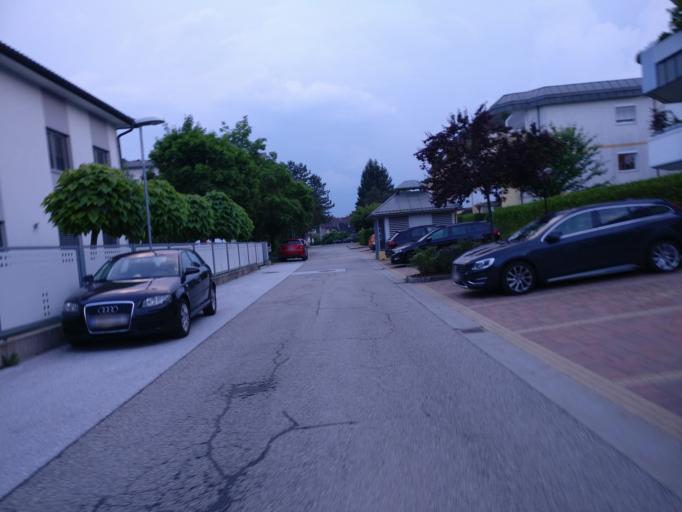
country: AT
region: Carinthia
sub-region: Klagenfurt am Woerthersee
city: Klagenfurt am Woerthersee
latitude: 46.6065
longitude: 14.2959
